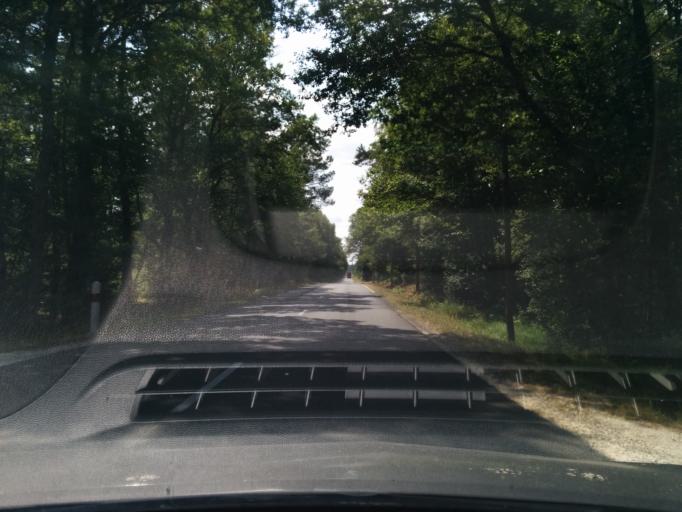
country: FR
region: Centre
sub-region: Departement du Cher
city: Neuvy-sur-Barangeon
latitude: 47.3216
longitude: 2.2892
